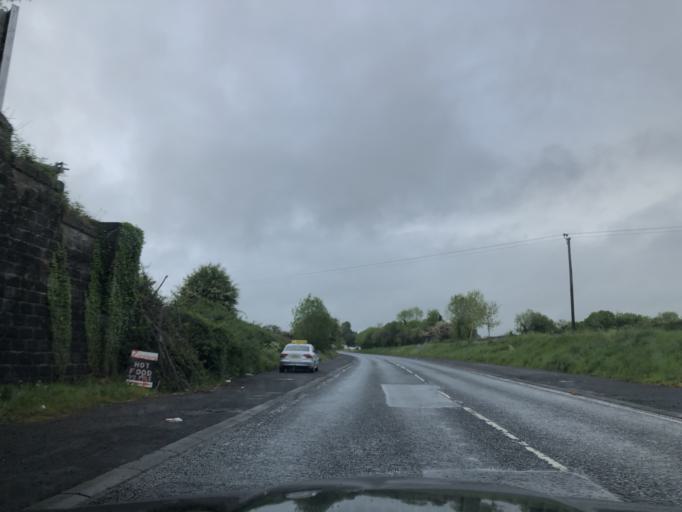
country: GB
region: Northern Ireland
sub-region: Antrim Borough
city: Antrim
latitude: 54.7373
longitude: -6.2327
